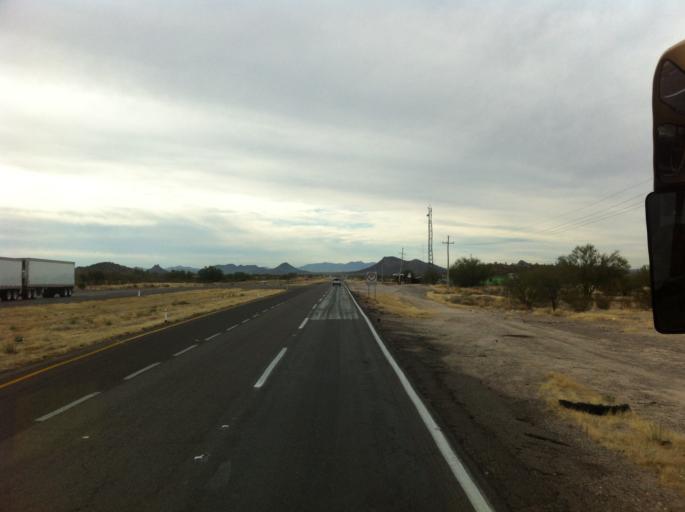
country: MX
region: Sonora
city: Hermosillo
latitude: 28.9627
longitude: -110.9634
